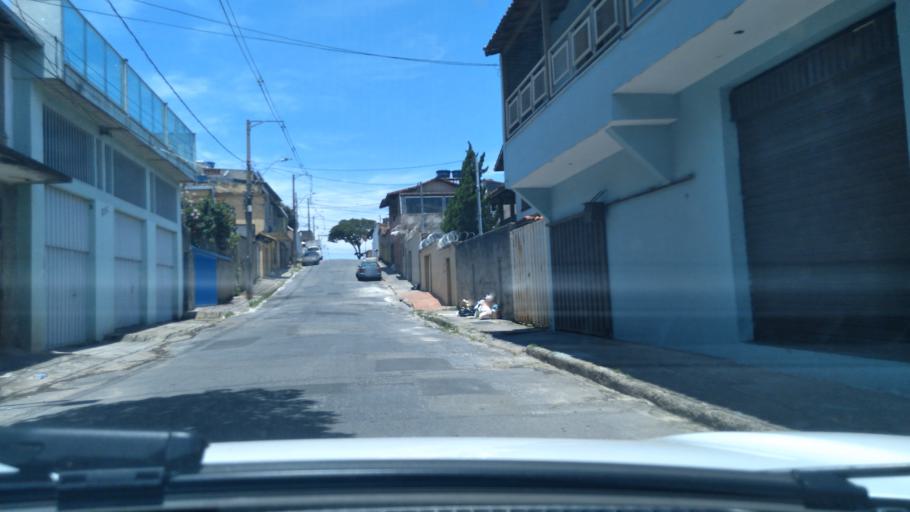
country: BR
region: Minas Gerais
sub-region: Contagem
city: Contagem
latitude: -19.9348
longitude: -44.0012
